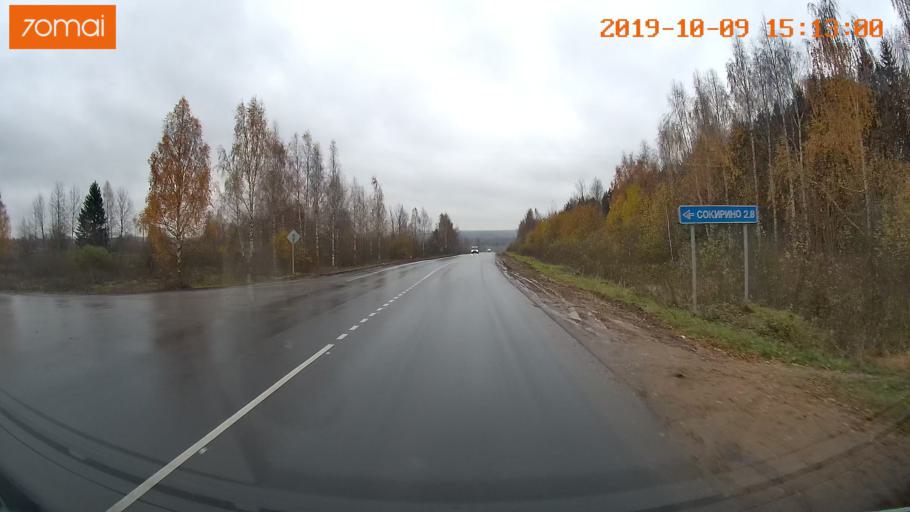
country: RU
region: Kostroma
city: Susanino
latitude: 58.1512
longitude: 41.6149
